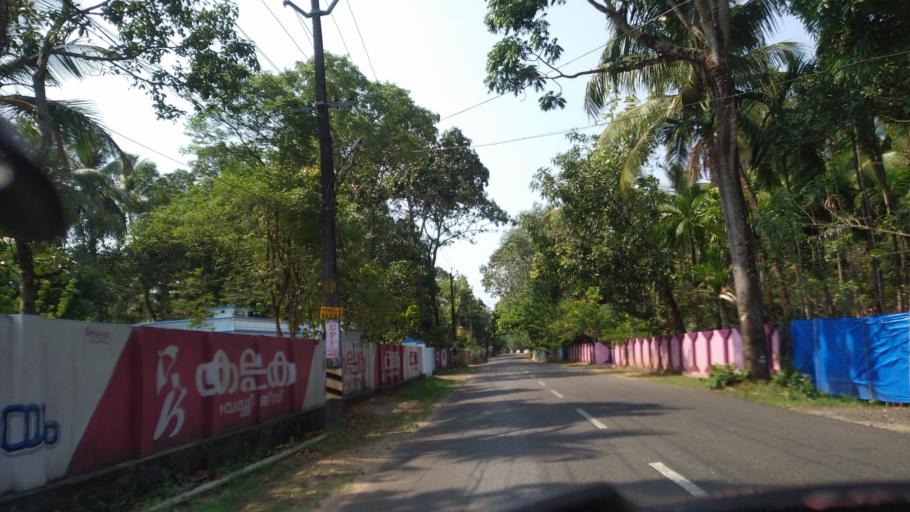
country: IN
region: Kerala
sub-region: Thrissur District
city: Thanniyam
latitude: 10.3373
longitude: 76.1185
